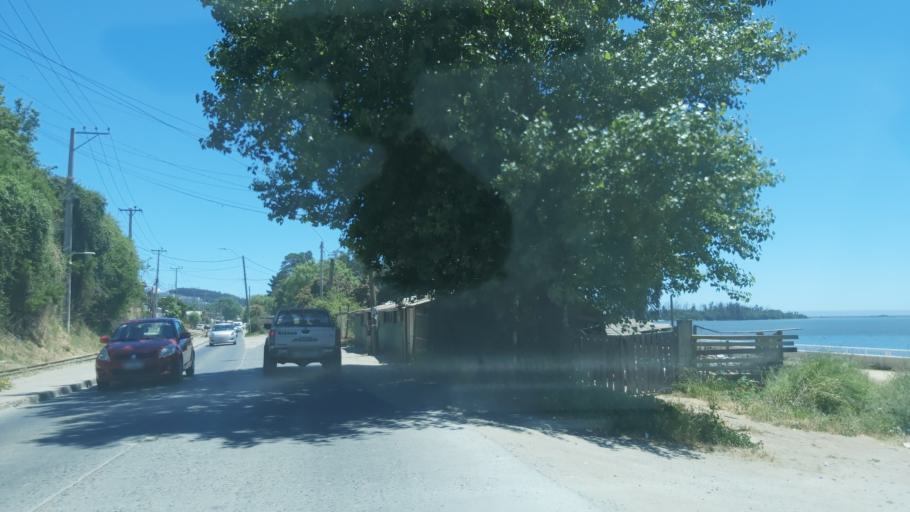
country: CL
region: Maule
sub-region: Provincia de Talca
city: Constitucion
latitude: -35.3403
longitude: -72.3968
